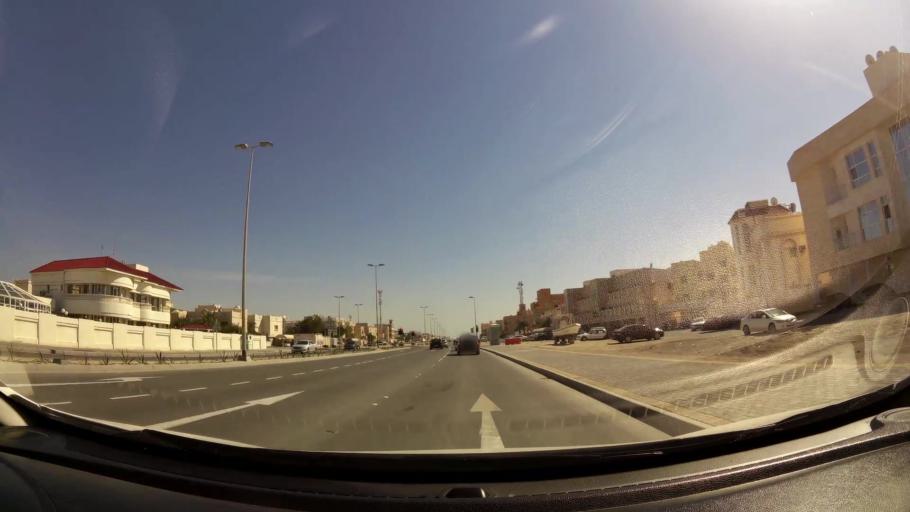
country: BH
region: Muharraq
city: Al Hadd
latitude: 26.2518
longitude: 50.6397
